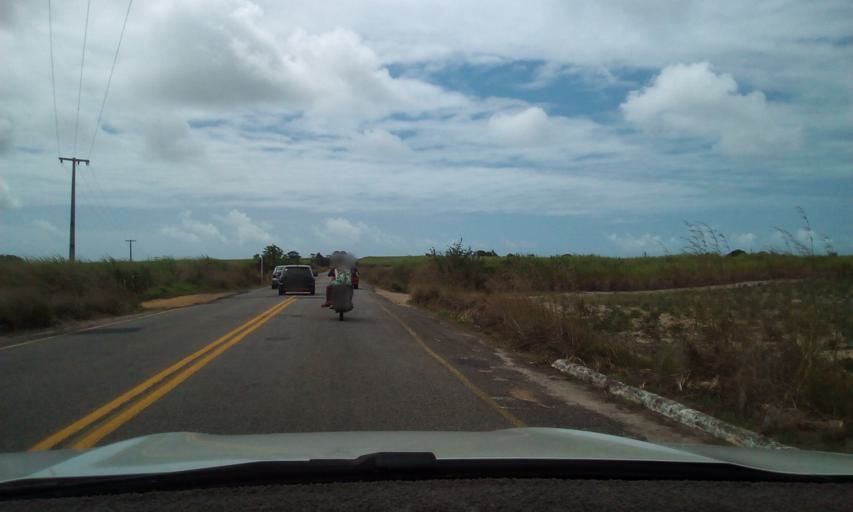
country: BR
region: Paraiba
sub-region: Rio Tinto
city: Rio Tinto
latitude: -6.7606
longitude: -34.9993
